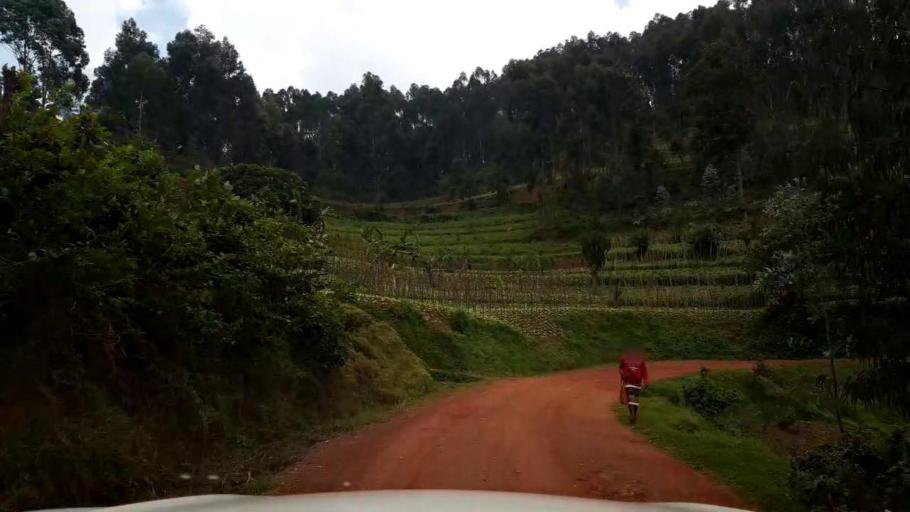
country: RW
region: Northern Province
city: Byumba
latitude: -1.5265
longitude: 29.9612
